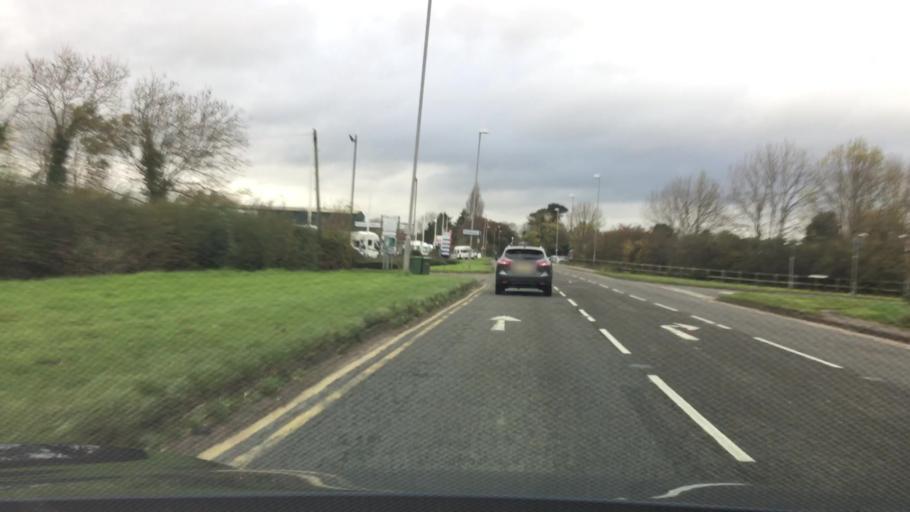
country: GB
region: England
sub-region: Nottinghamshire
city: Lowdham
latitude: 52.9929
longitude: -0.9917
